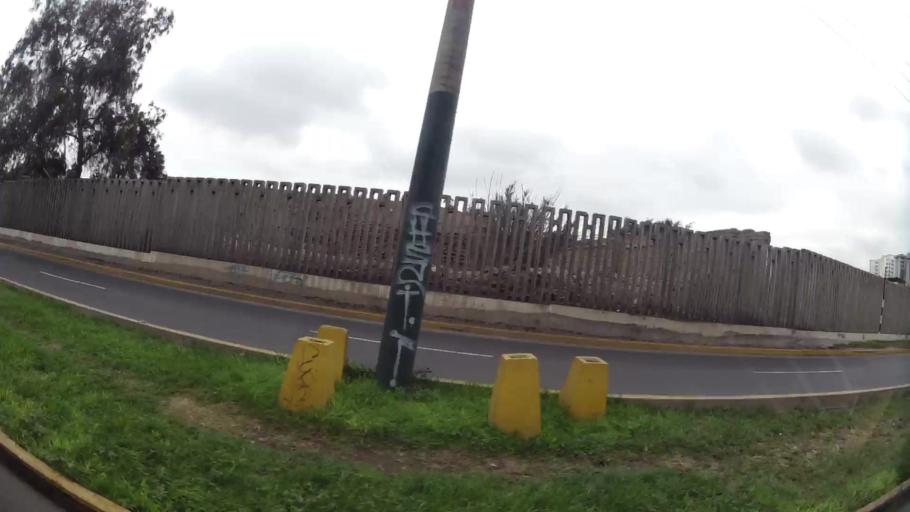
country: PE
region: Lima
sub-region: Lima
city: Surco
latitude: -12.1608
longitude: -76.9895
